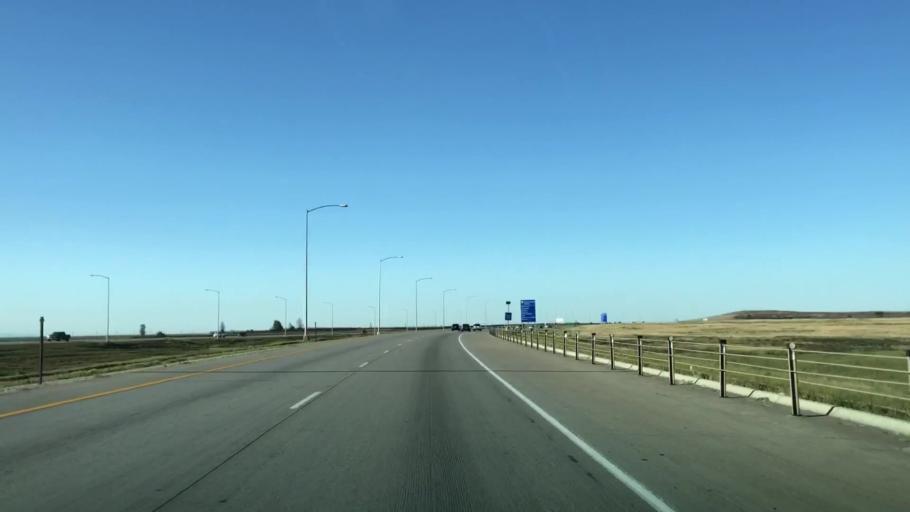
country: US
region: Colorado
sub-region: Adams County
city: Aurora
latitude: 39.8189
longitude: -104.7865
